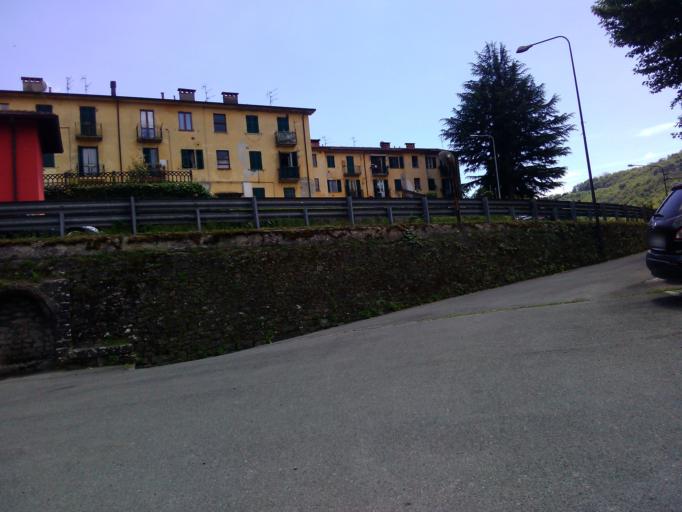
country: IT
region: Tuscany
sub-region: Provincia di Massa-Carrara
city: Villafranca in Lunigiana
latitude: 44.2895
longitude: 9.9482
